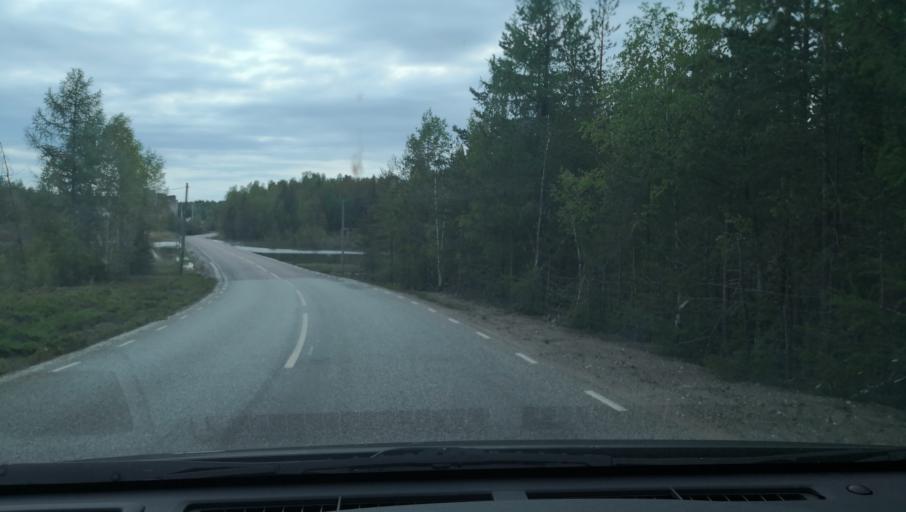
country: SE
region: Vaestmanland
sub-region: Skinnskattebergs Kommun
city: Skinnskatteberg
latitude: 59.8336
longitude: 15.5728
